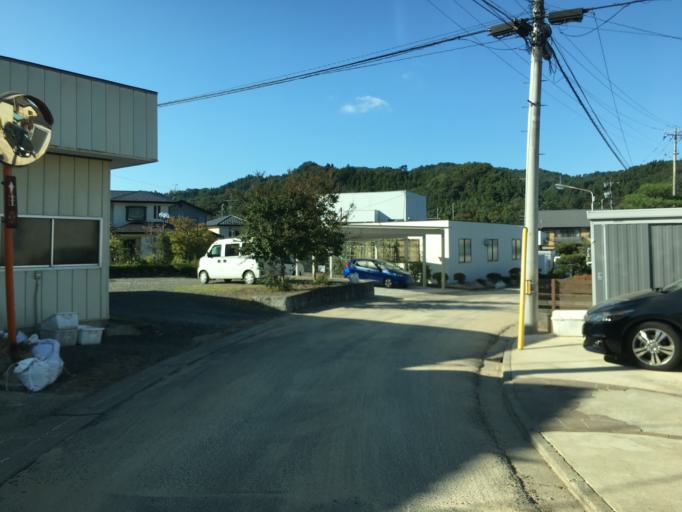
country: JP
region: Fukushima
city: Hobaramachi
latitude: 37.6659
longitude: 140.6085
